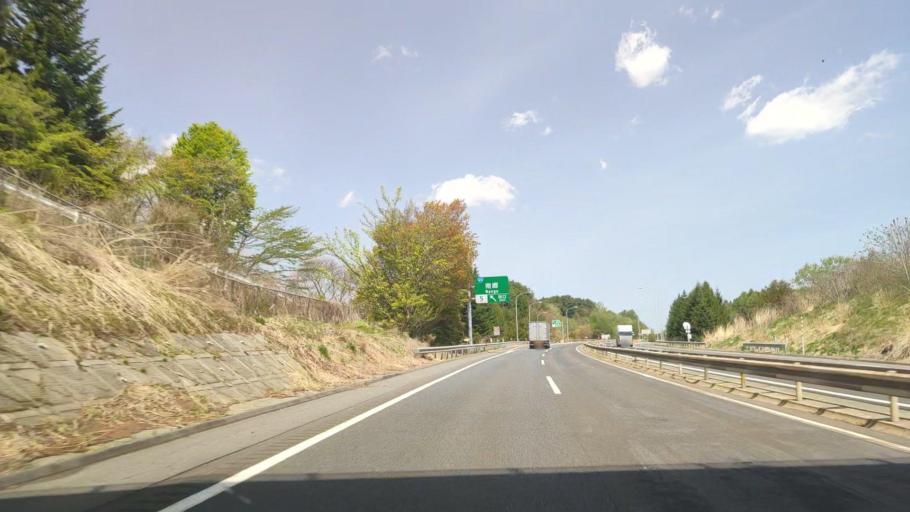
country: JP
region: Aomori
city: Hachinohe
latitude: 40.4034
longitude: 141.4437
